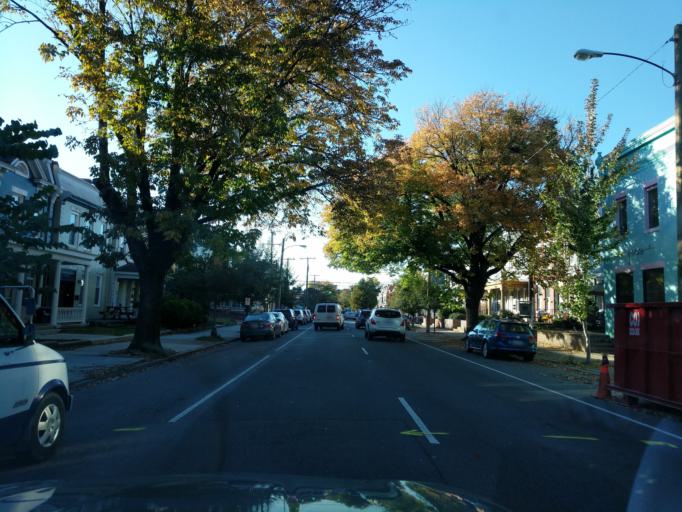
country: US
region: Virginia
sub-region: City of Richmond
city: Richmond
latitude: 37.5514
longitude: -77.4721
